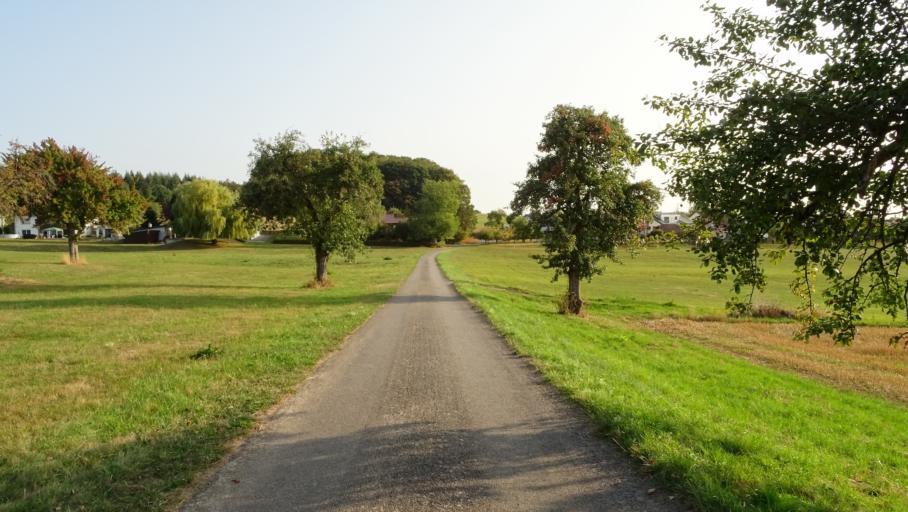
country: DE
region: Baden-Wuerttemberg
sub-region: Karlsruhe Region
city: Fahrenbach
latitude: 49.4294
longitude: 9.1403
